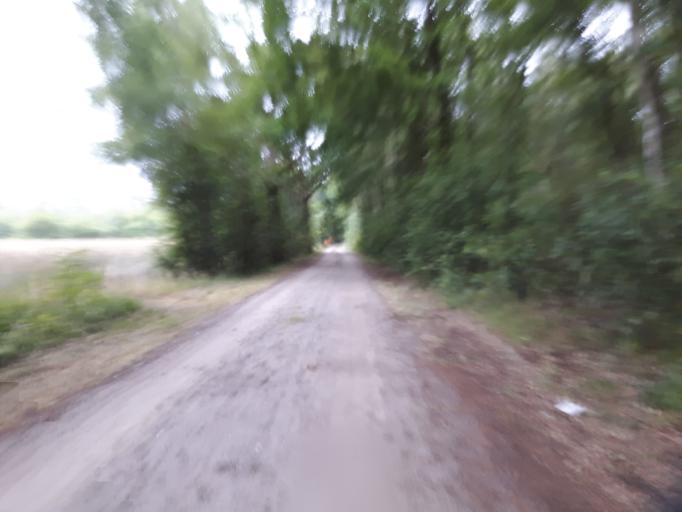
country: DE
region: Lower Saxony
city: Garstedt
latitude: 53.3138
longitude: 10.1963
